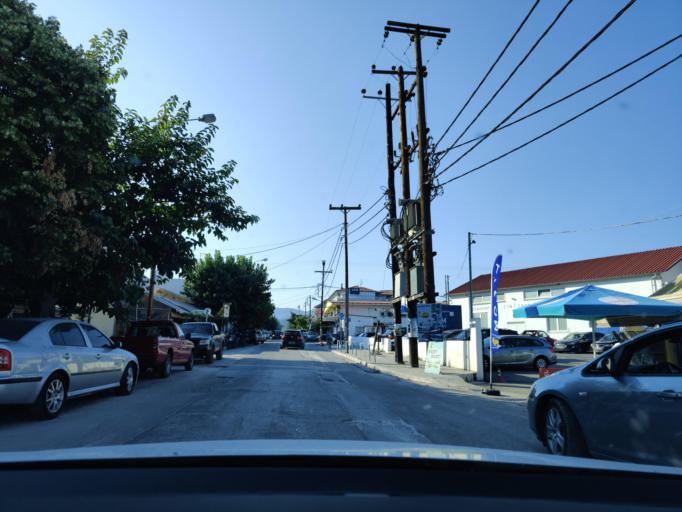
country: GR
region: East Macedonia and Thrace
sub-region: Nomos Kavalas
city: Limenaria
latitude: 40.6104
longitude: 24.6074
